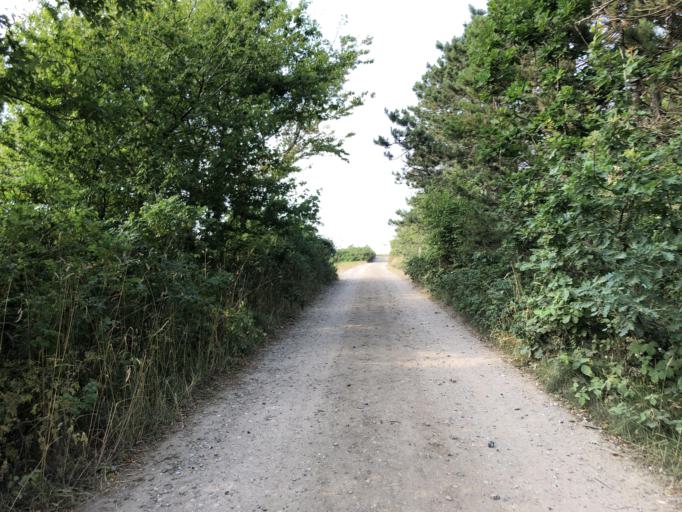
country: DK
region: Zealand
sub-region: Odsherred Kommune
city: Hojby
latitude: 55.9501
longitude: 11.5191
